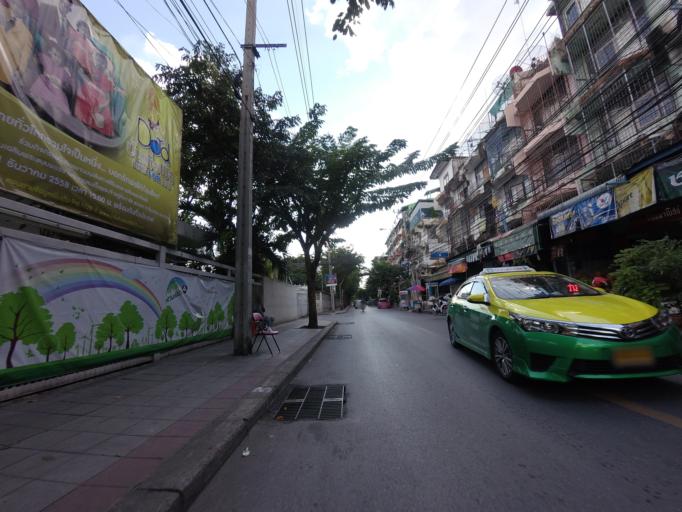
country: TH
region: Bangkok
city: Bang Sue
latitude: 13.8031
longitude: 100.5563
